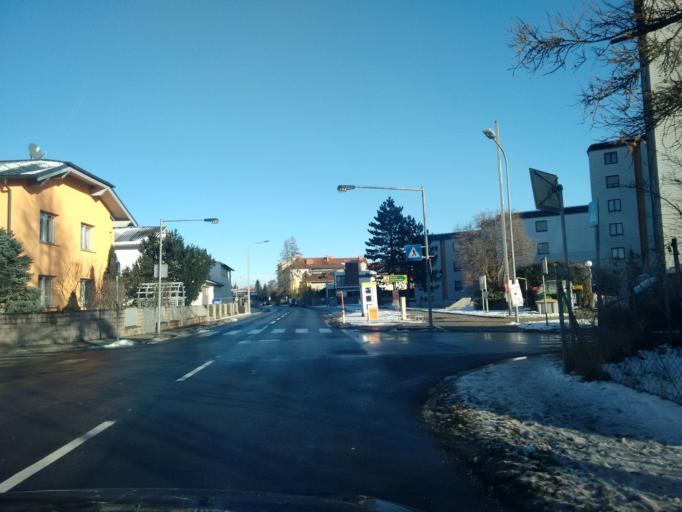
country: AT
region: Upper Austria
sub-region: Politischer Bezirk Linz-Land
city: Traun
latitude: 48.2282
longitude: 14.2410
